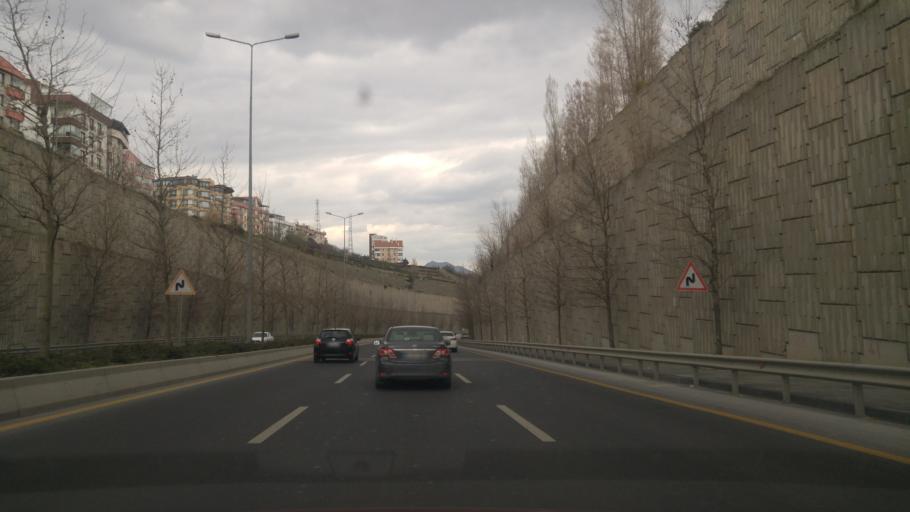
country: TR
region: Ankara
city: Cankaya
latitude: 39.8847
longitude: 32.8891
